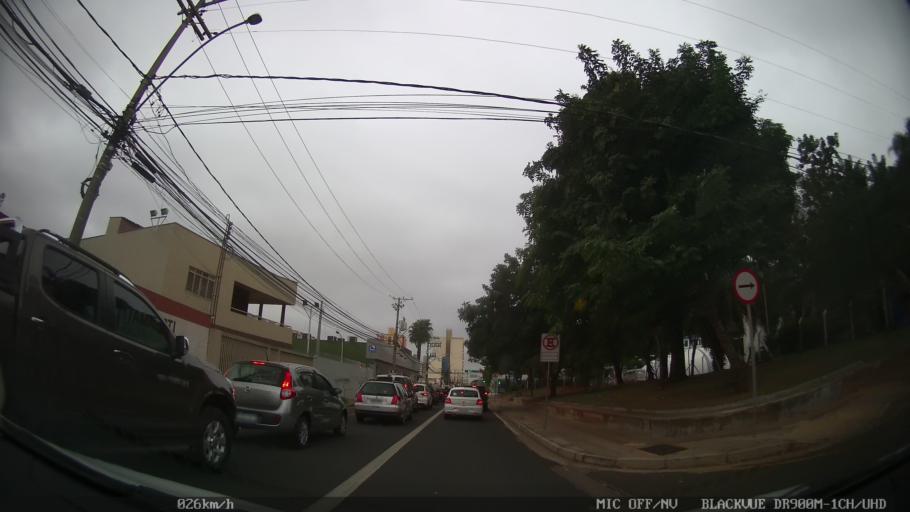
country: BR
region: Sao Paulo
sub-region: Sao Jose Do Rio Preto
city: Sao Jose do Rio Preto
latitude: -20.8215
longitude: -49.3916
